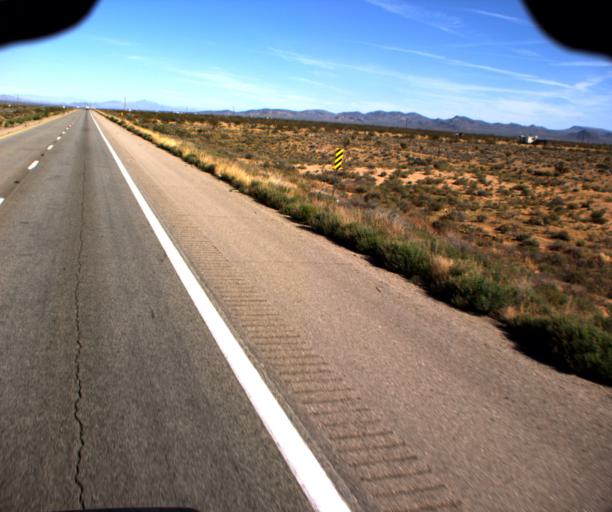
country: US
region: Arizona
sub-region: Mohave County
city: Dolan Springs
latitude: 35.4989
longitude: -114.3309
